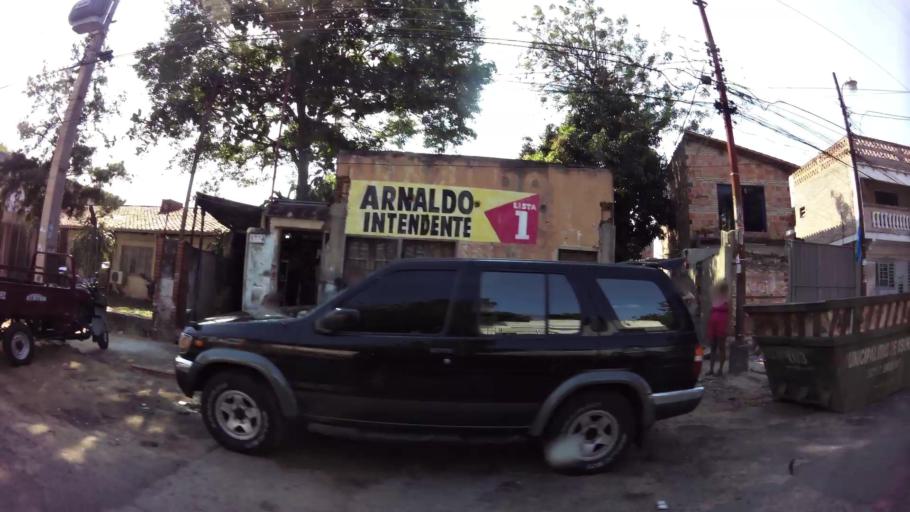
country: PY
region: Asuncion
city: Asuncion
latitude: -25.3099
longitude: -57.6246
